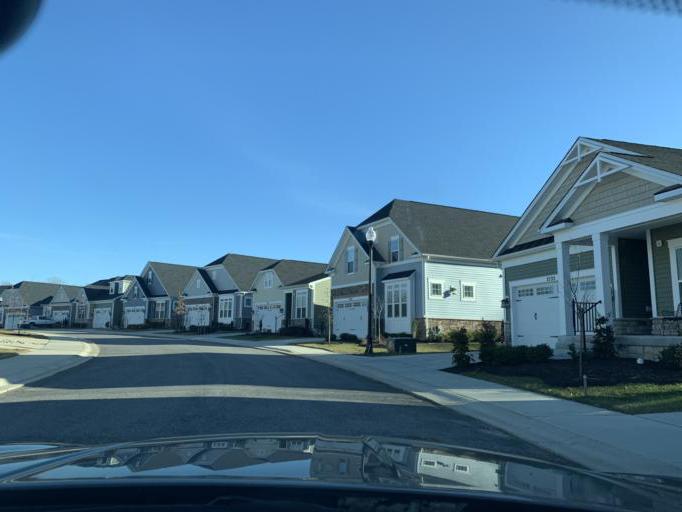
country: US
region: Maryland
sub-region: Anne Arundel County
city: Crofton
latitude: 39.0144
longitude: -76.7219
